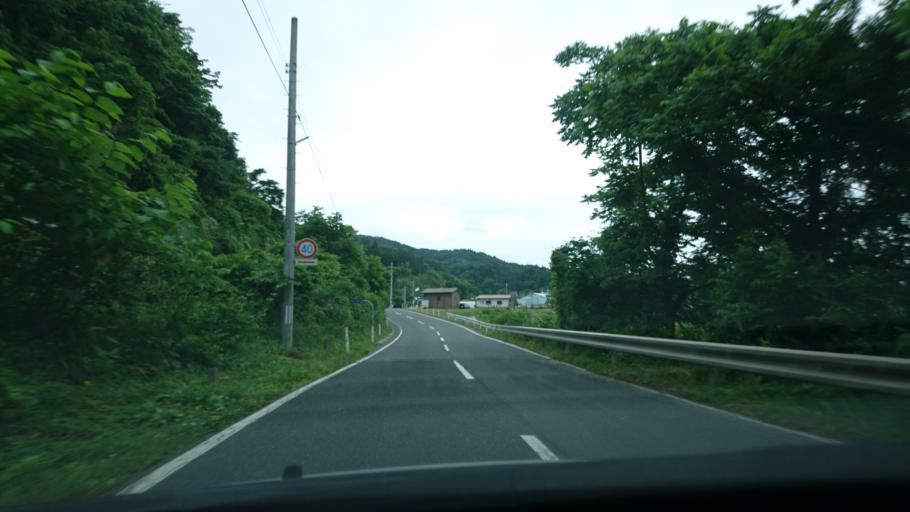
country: JP
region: Iwate
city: Ichinoseki
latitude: 38.9727
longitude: 141.2382
